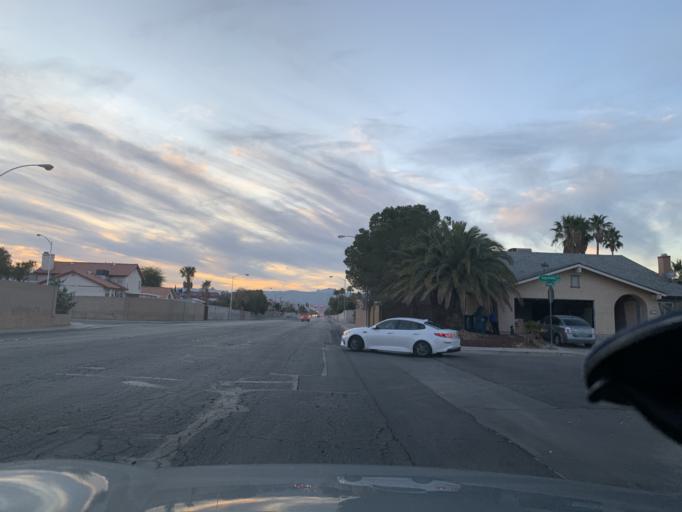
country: US
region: Nevada
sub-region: Clark County
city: Spring Valley
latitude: 36.0926
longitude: -115.2312
